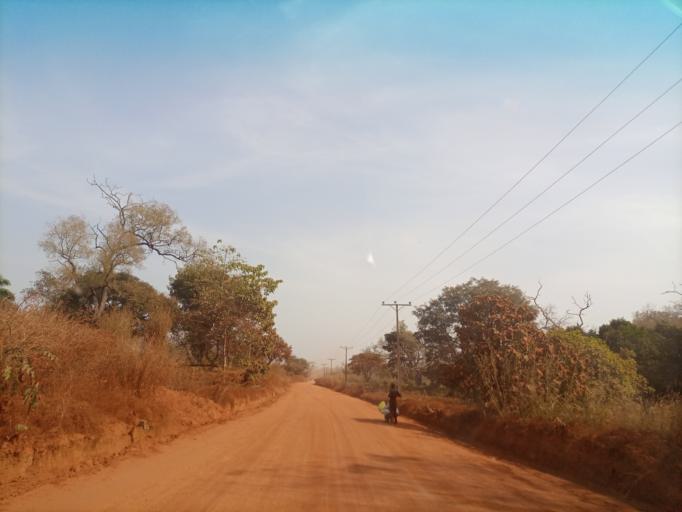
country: NG
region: Enugu
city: Eha Amufu
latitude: 6.6733
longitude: 7.7338
